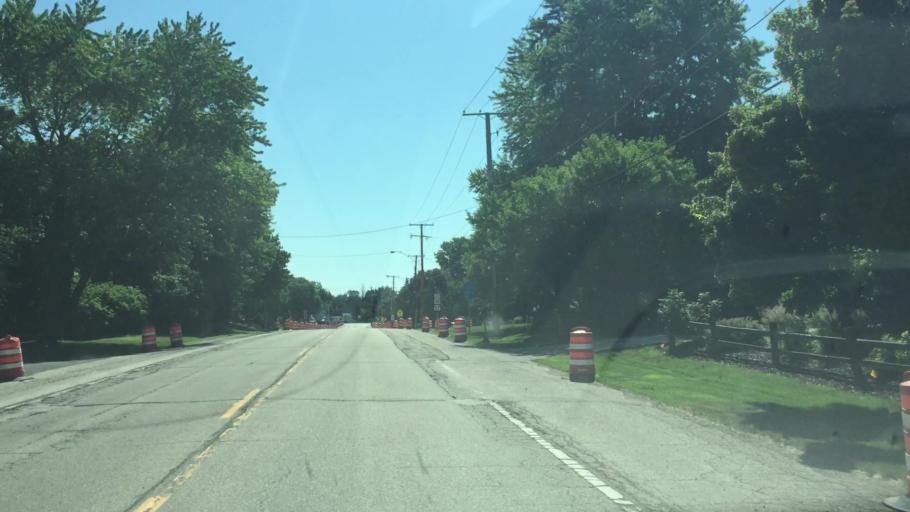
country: US
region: Wisconsin
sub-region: Calumet County
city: Hilbert
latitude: 44.1400
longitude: -88.1690
